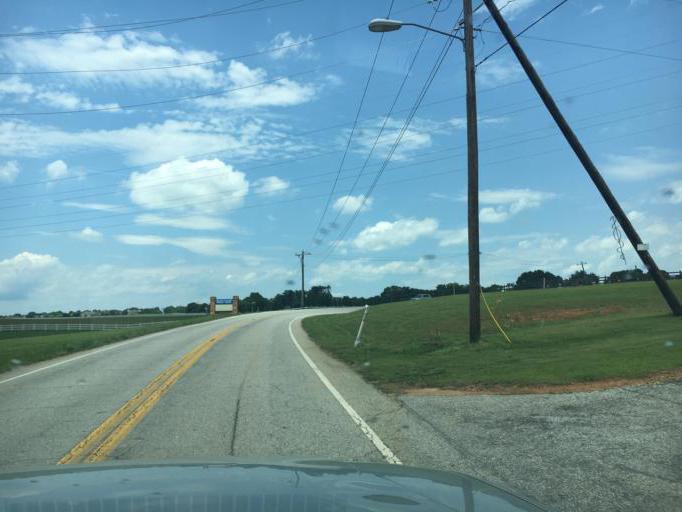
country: US
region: South Carolina
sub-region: Greenville County
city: Greer
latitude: 34.8742
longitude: -82.2420
